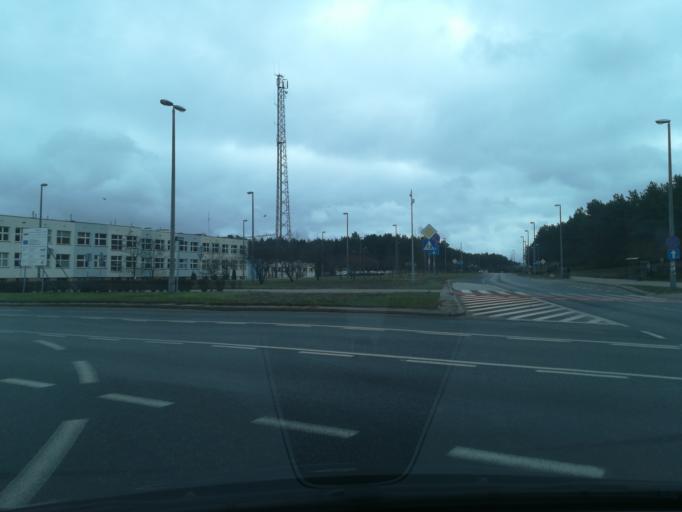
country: PL
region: Kujawsko-Pomorskie
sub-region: Powiat torunski
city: Lubicz Dolny
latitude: 53.0225
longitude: 18.6890
